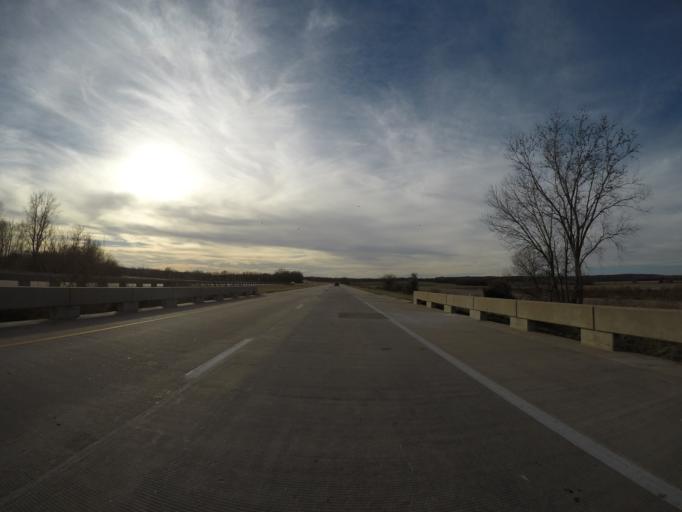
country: US
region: Kansas
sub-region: Franklin County
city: Ottawa
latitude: 38.5569
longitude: -95.3375
